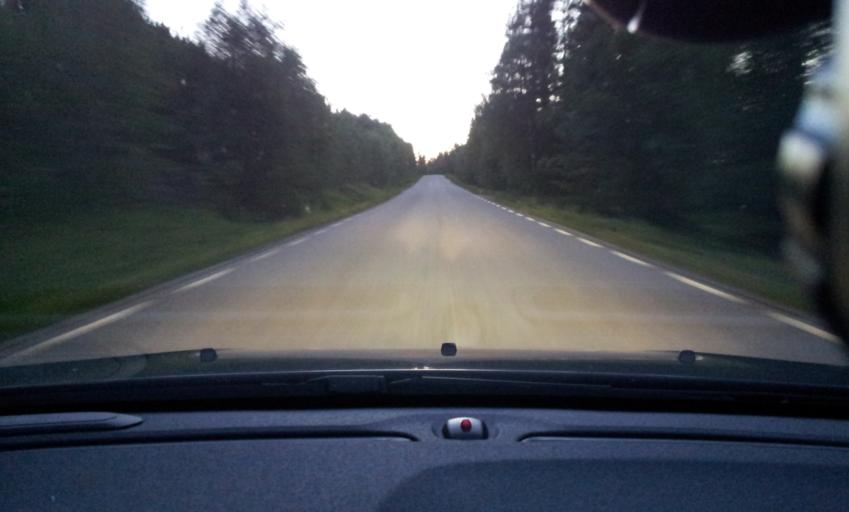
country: SE
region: Jaemtland
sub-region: Braecke Kommun
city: Braecke
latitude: 62.7263
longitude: 15.4102
